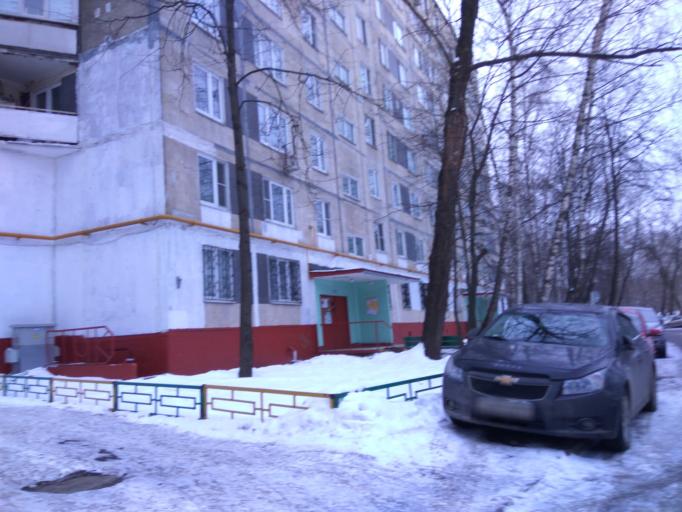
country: RU
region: Moscow
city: Ivanovskoye
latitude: 55.7718
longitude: 37.8251
